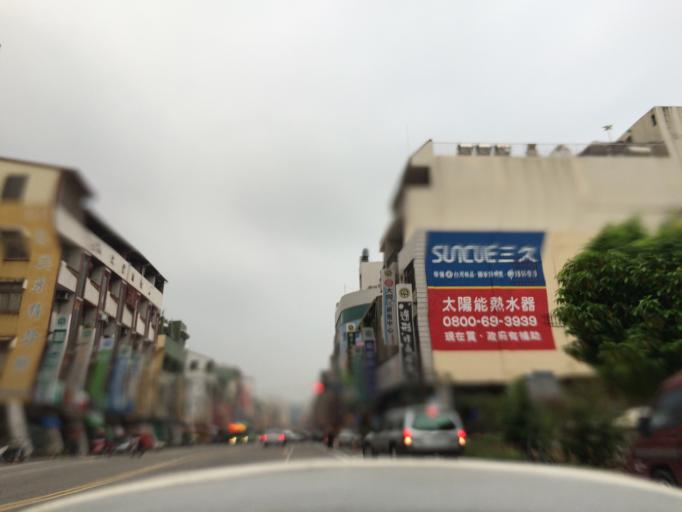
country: TW
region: Taiwan
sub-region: Taichung City
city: Taichung
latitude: 24.0685
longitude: 120.6991
